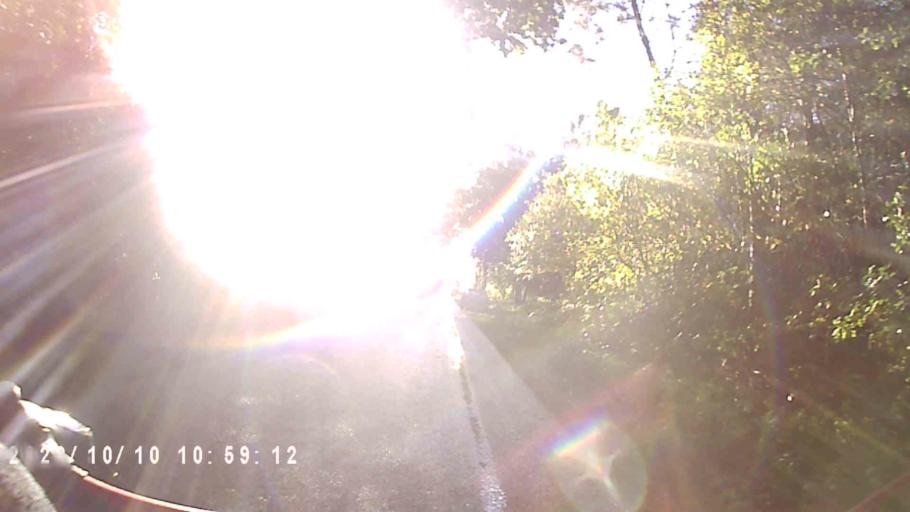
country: NL
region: Friesland
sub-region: Gemeente Achtkarspelen
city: Surhuisterveen
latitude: 53.1428
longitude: 6.2088
